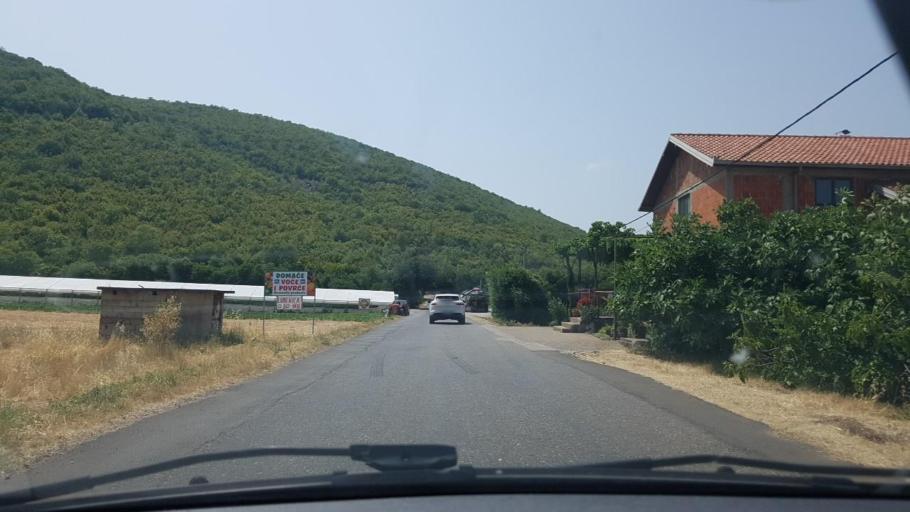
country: BA
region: Federation of Bosnia and Herzegovina
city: Tasovcici
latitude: 43.0342
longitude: 17.7289
